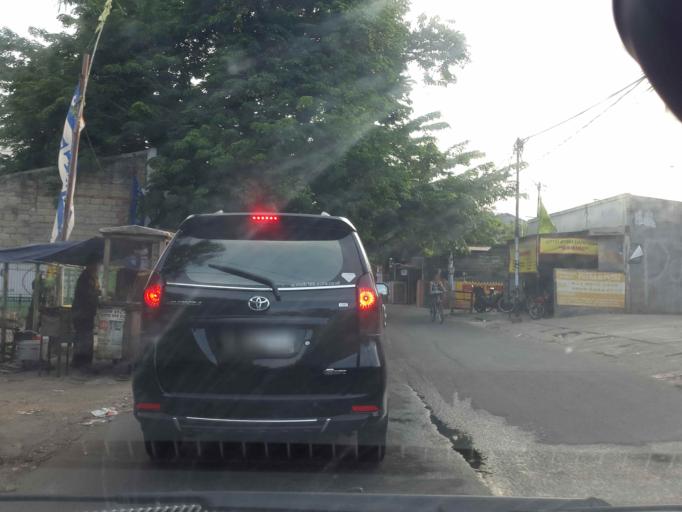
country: ID
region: Banten
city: South Tangerang
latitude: -6.2673
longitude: 106.7434
